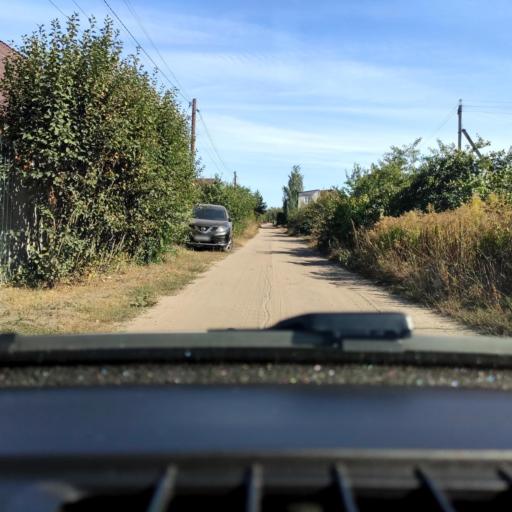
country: RU
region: Voronezj
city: Maslovka
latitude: 51.5255
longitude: 39.2320
